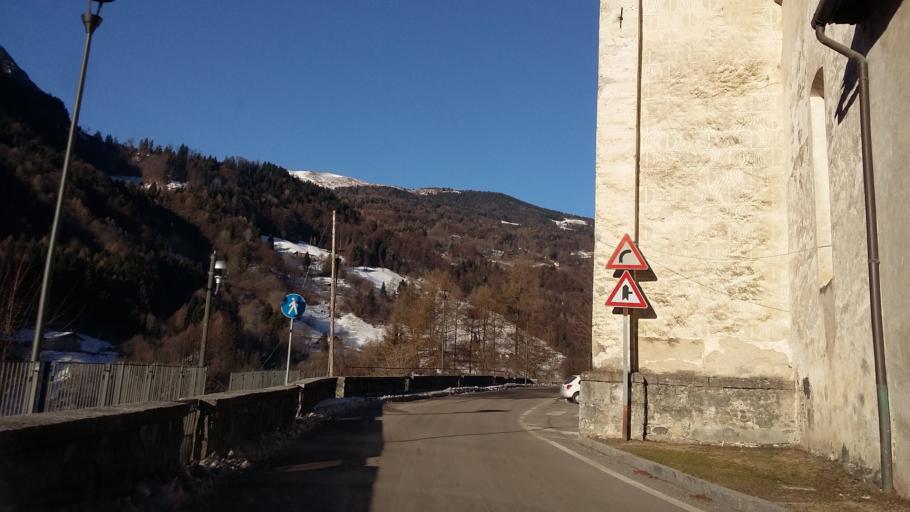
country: IT
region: Lombardy
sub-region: Provincia di Brescia
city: Bagolino
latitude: 45.8256
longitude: 10.4597
